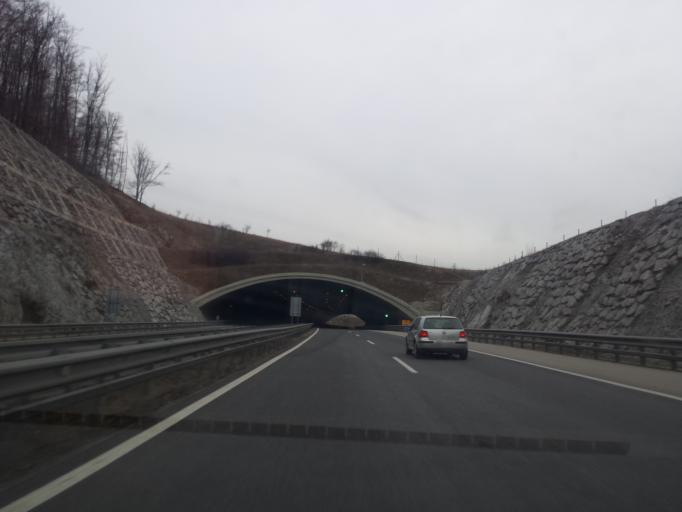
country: SI
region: Novo Mesto
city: Novo Mesto
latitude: 45.8510
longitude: 15.1454
